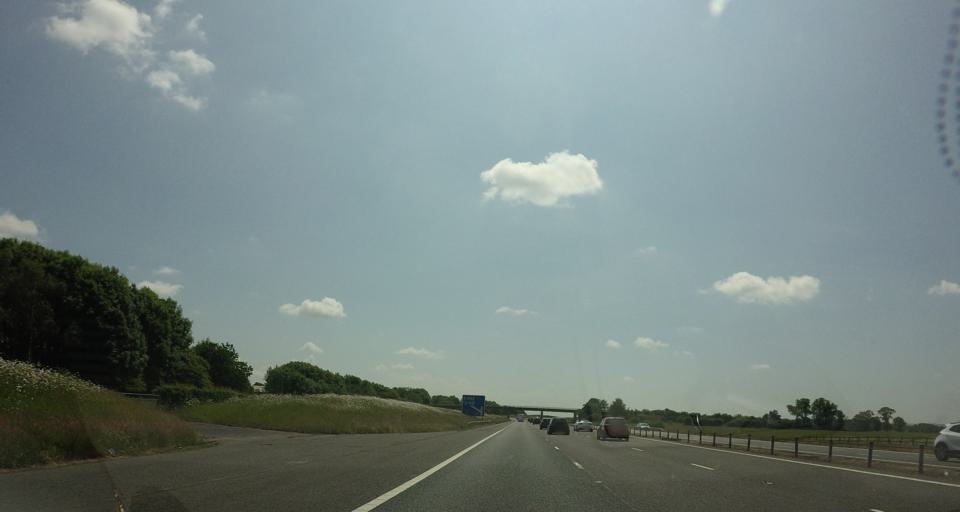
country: GB
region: Scotland
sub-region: Dumfries and Galloway
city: Lockerbie
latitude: 55.1525
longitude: -3.3831
